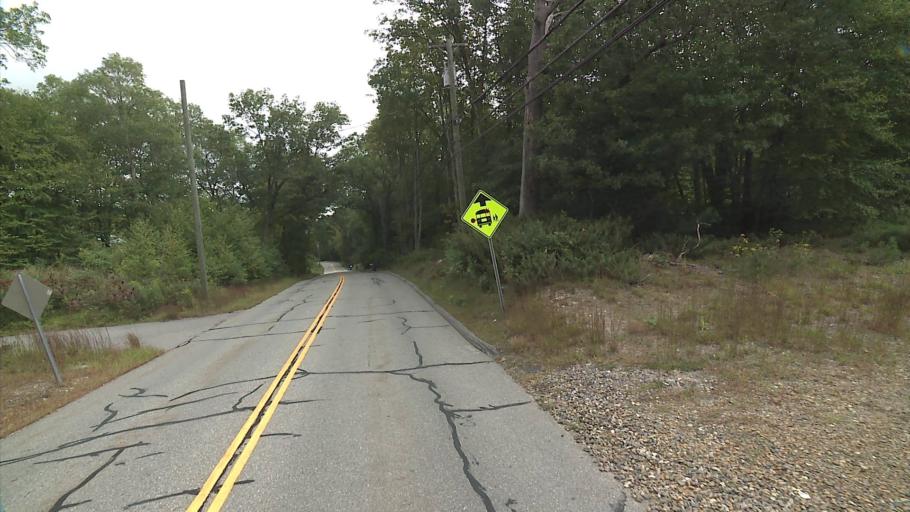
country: US
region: Connecticut
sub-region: Tolland County
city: South Coventry
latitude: 41.7754
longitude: -72.2875
